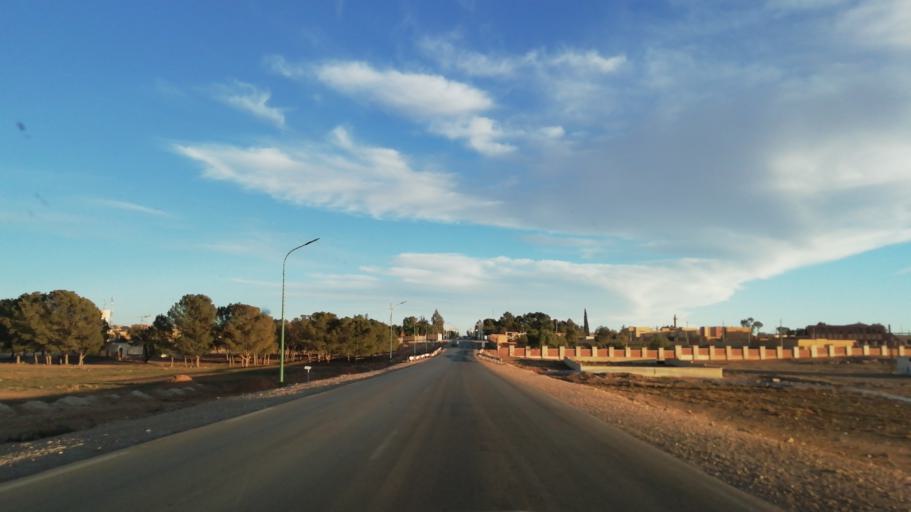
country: DZ
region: Wilaya de Naama
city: Naama
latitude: 33.7211
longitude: -0.7348
